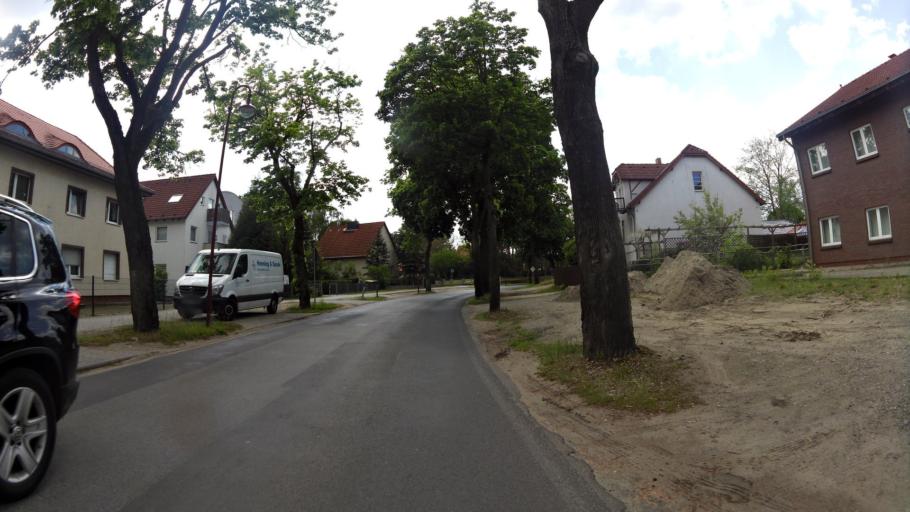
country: DE
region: Brandenburg
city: Gross Koris
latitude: 52.1606
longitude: 13.6586
